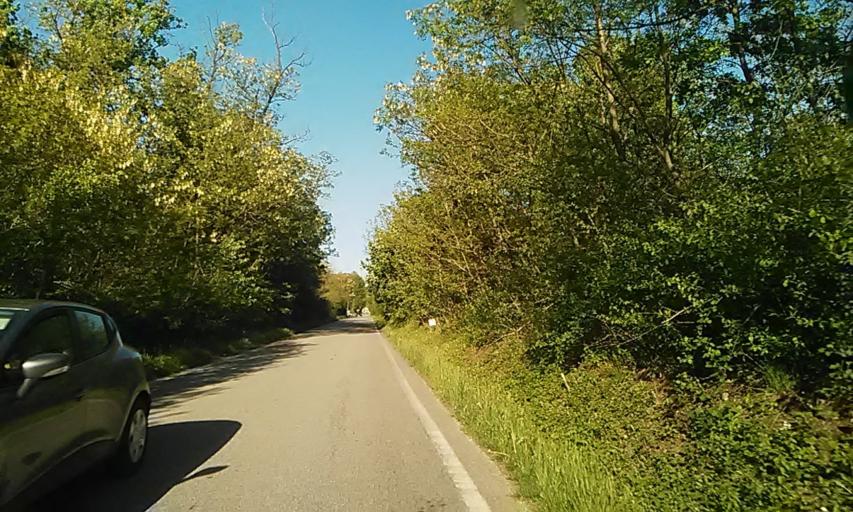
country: IT
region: Piedmont
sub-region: Provincia di Novara
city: Cavaglietto
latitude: 45.6152
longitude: 8.5030
